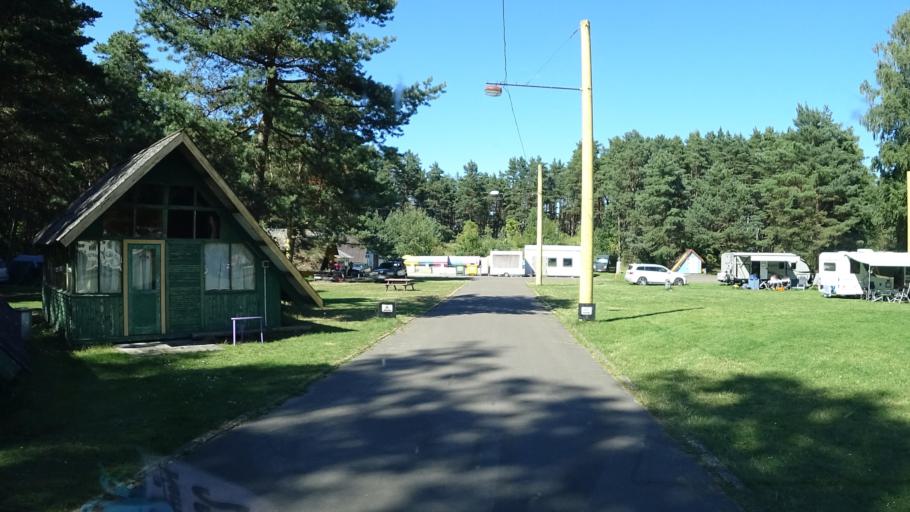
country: LV
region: Jurmala
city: Jurmala
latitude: 56.9605
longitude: 23.6454
